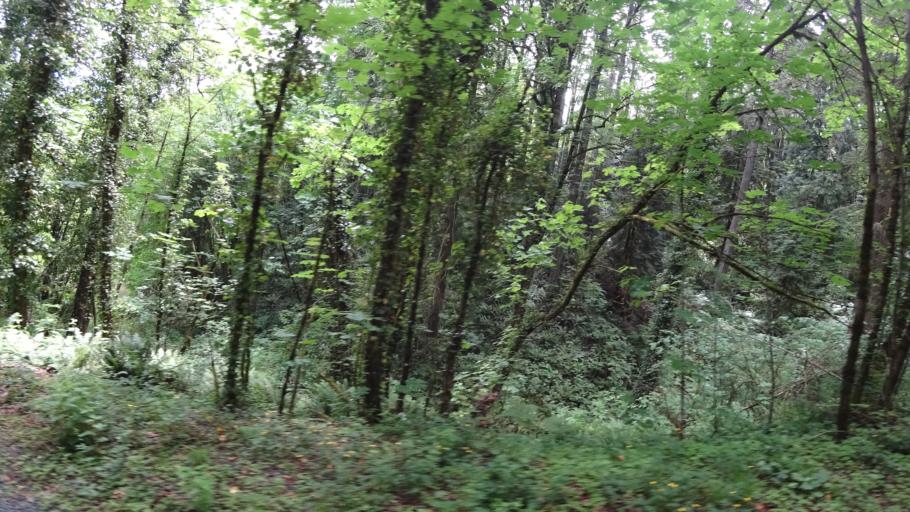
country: US
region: Oregon
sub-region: Washington County
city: West Haven
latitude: 45.5841
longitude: -122.7783
